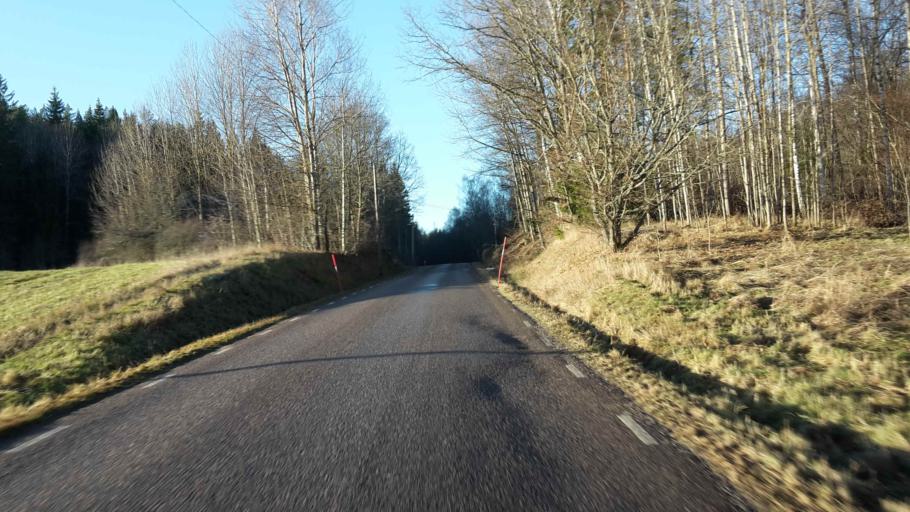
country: SE
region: Kalmar
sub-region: Vasterviks Kommun
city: Overum
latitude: 58.1538
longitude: 16.2980
